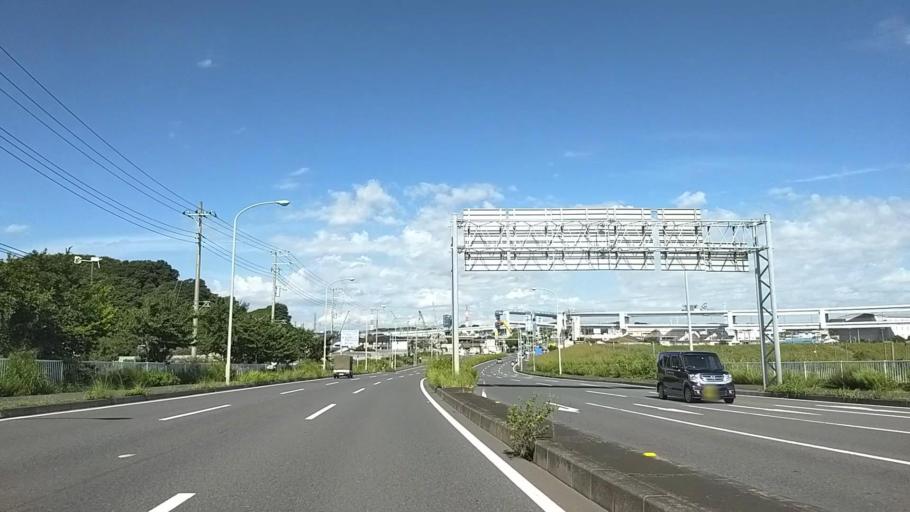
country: JP
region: Kanagawa
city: Yokohama
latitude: 35.5128
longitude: 139.5995
